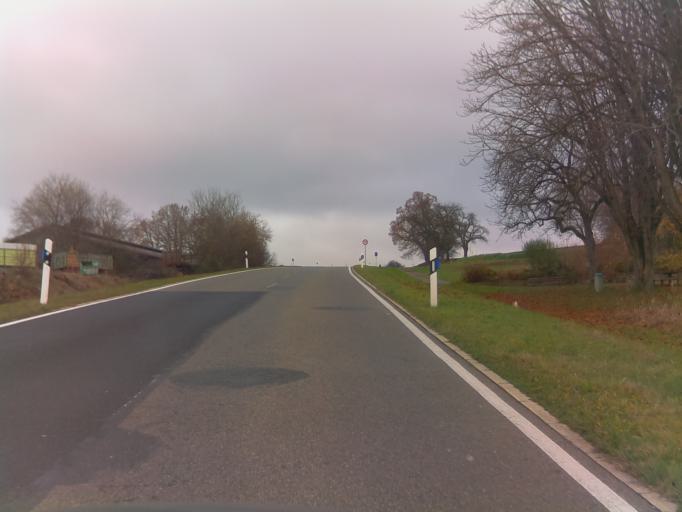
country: DE
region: Baden-Wuerttemberg
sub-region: Karlsruhe Region
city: Neckargerach
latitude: 49.4290
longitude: 9.0822
